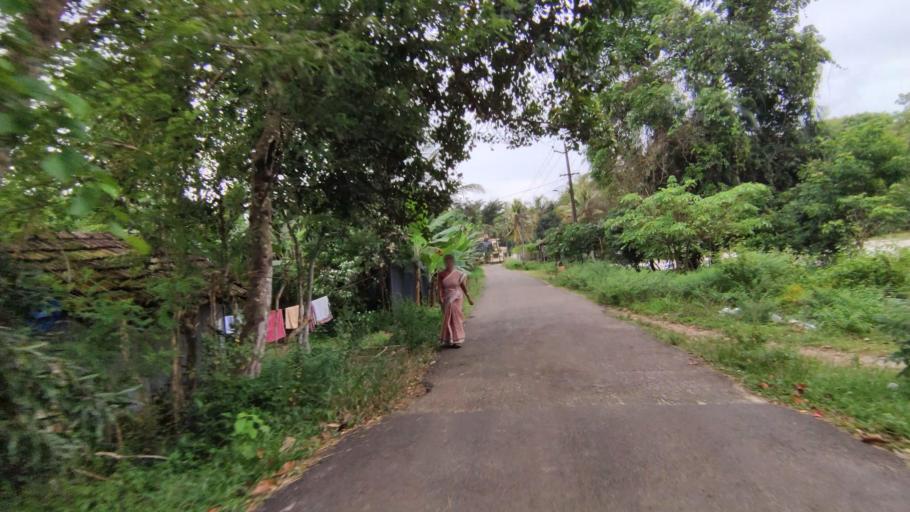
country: IN
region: Kerala
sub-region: Alappuzha
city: Shertallai
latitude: 9.6281
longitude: 76.3575
